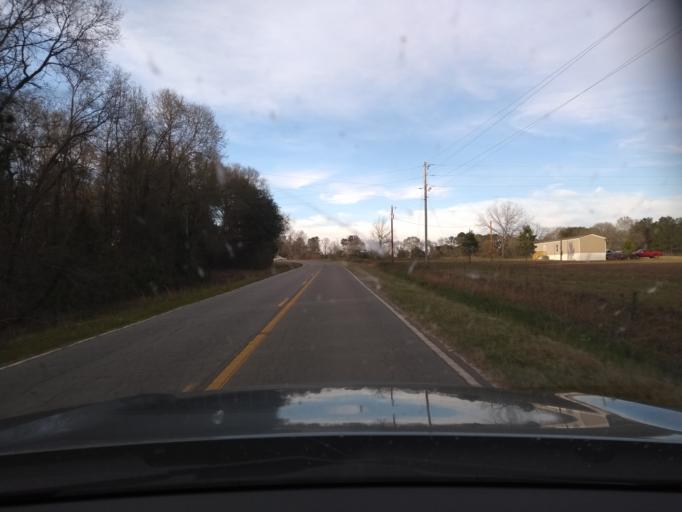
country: US
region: Georgia
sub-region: Evans County
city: Claxton
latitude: 32.2392
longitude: -81.7698
